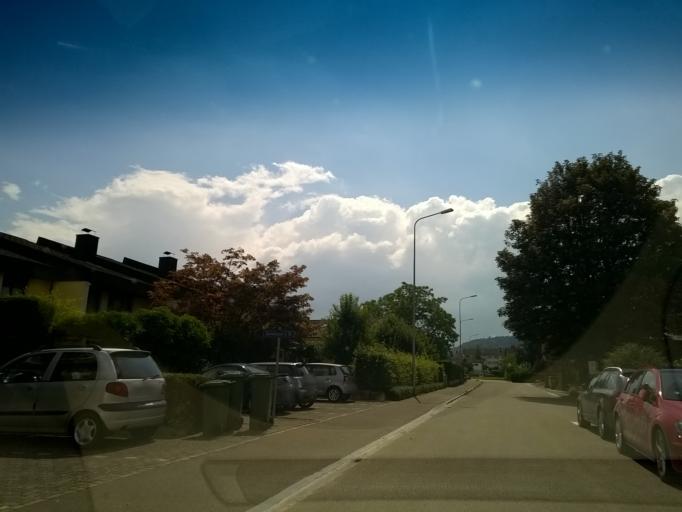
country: CH
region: Zurich
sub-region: Bezirk Buelach
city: Embrach / Embrach (Dorfkern)
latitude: 47.5037
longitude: 8.5980
